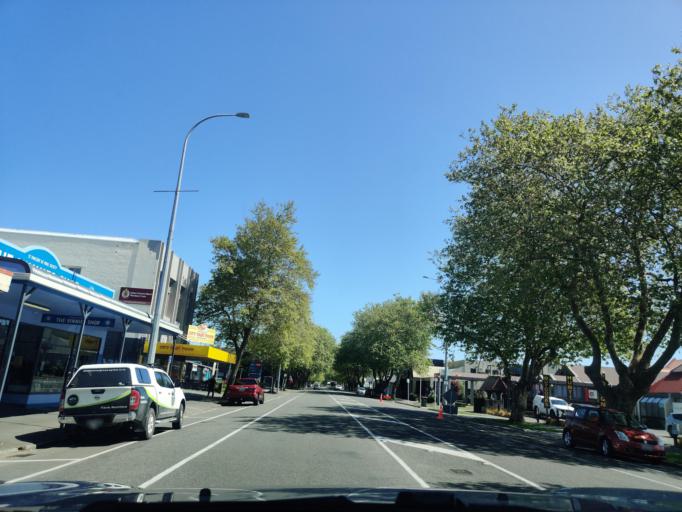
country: NZ
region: Manawatu-Wanganui
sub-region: Wanganui District
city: Wanganui
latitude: -39.9300
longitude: 175.0471
